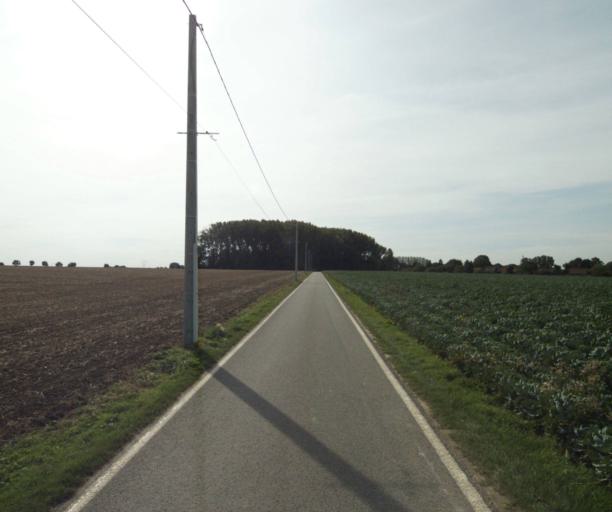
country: FR
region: Nord-Pas-de-Calais
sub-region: Departement du Nord
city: Ennetieres-en-Weppes
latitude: 50.6242
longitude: 2.9354
